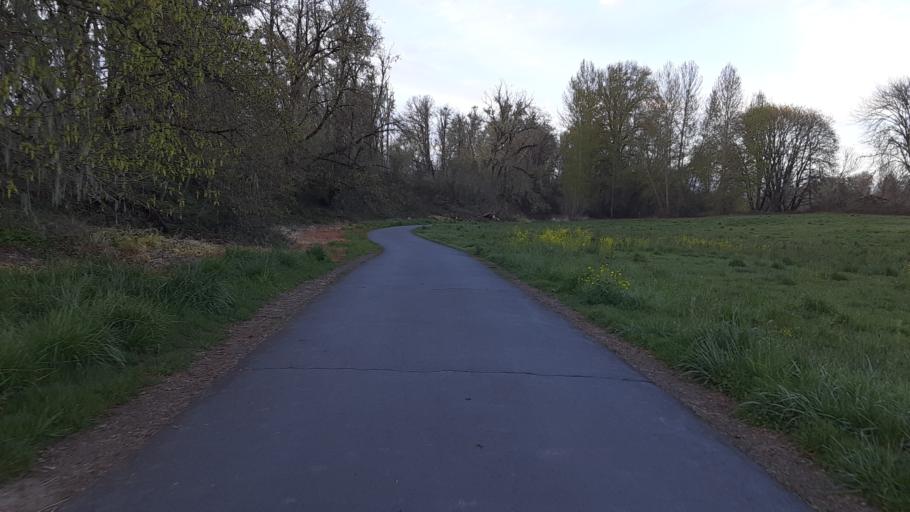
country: US
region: Oregon
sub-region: Benton County
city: Corvallis
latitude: 44.5312
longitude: -123.2532
